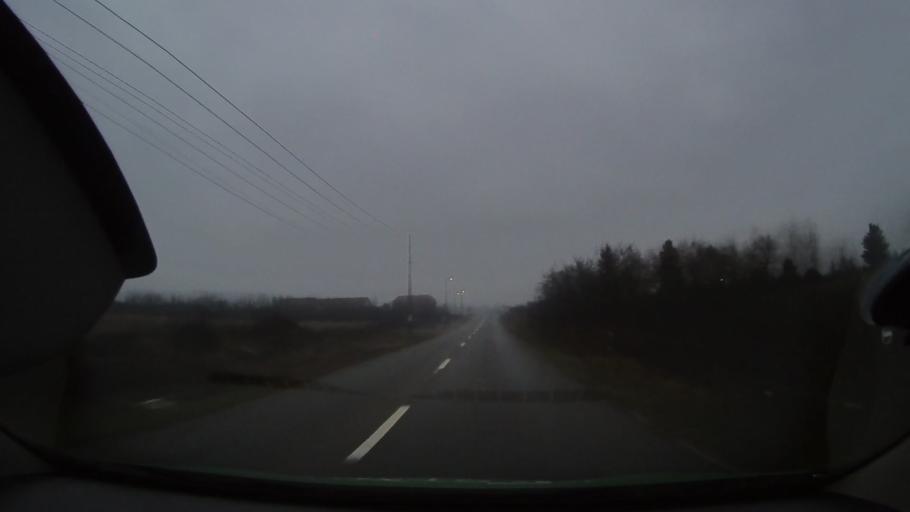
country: RO
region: Arad
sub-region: Comuna Beliu
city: Beliu
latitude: 46.4865
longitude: 21.9949
